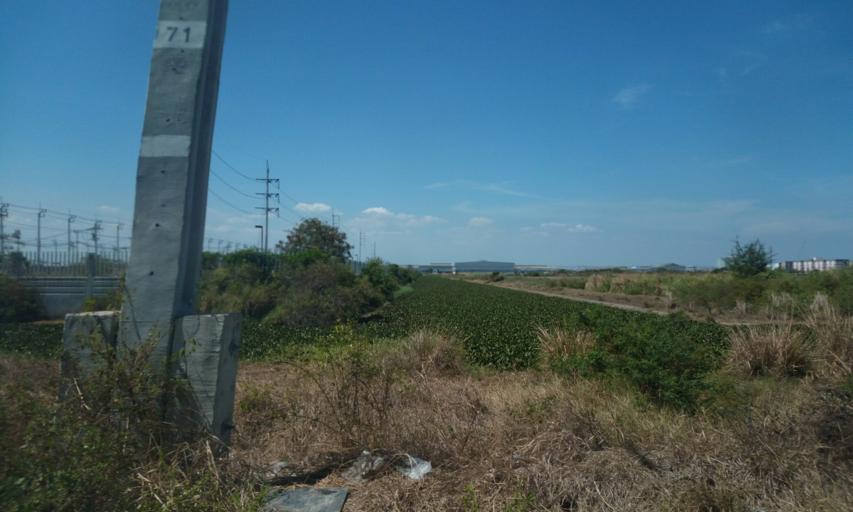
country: TH
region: Samut Prakan
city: Bang Bo District
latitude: 13.5555
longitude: 100.7731
